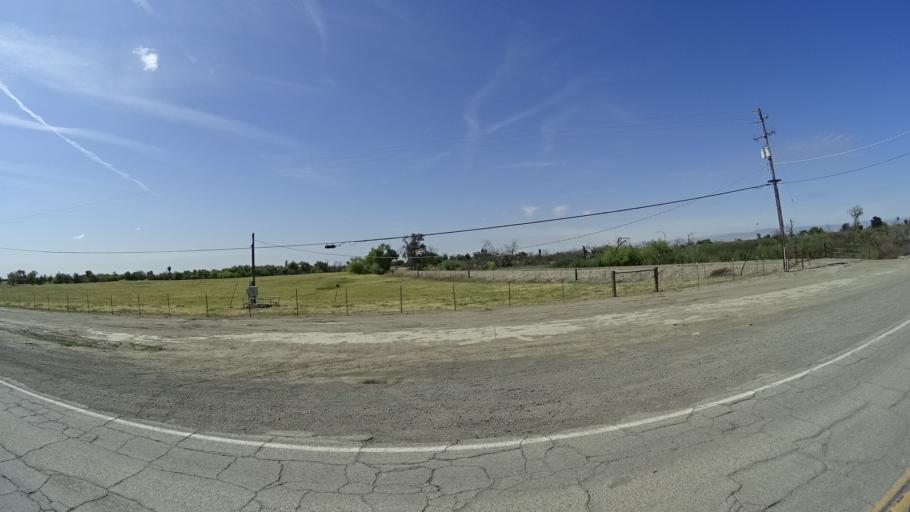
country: US
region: California
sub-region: Kings County
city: Lemoore Station
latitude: 36.2556
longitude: -119.8536
